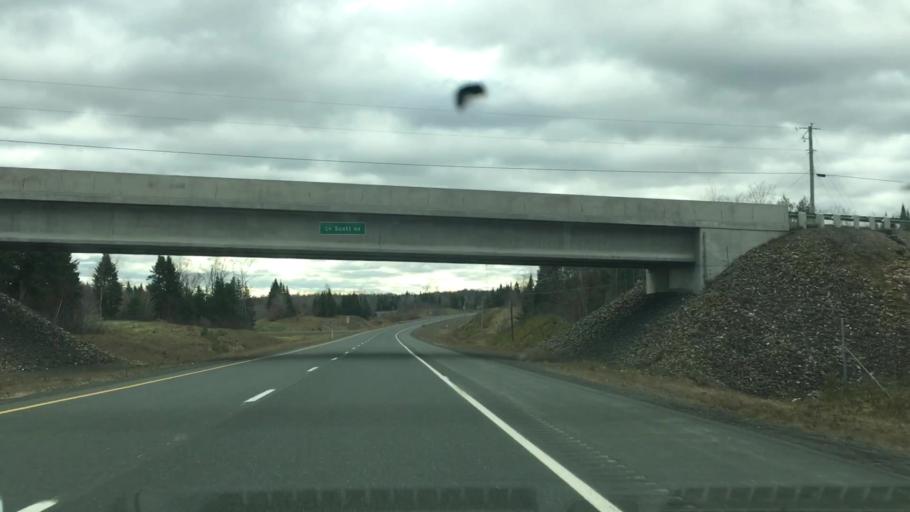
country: US
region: Maine
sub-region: Aroostook County
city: Easton
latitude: 46.6260
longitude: -67.7399
